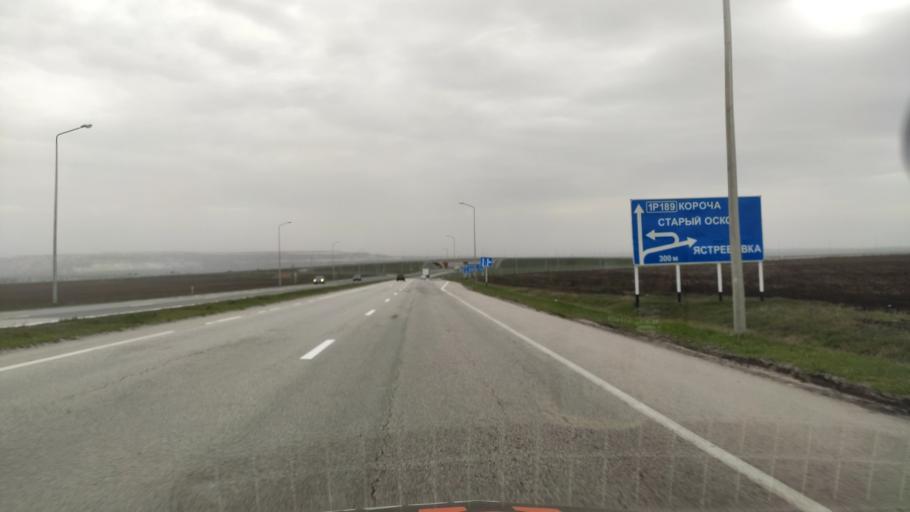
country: RU
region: Belgorod
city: Staryy Oskol
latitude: 51.3295
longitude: 37.7485
